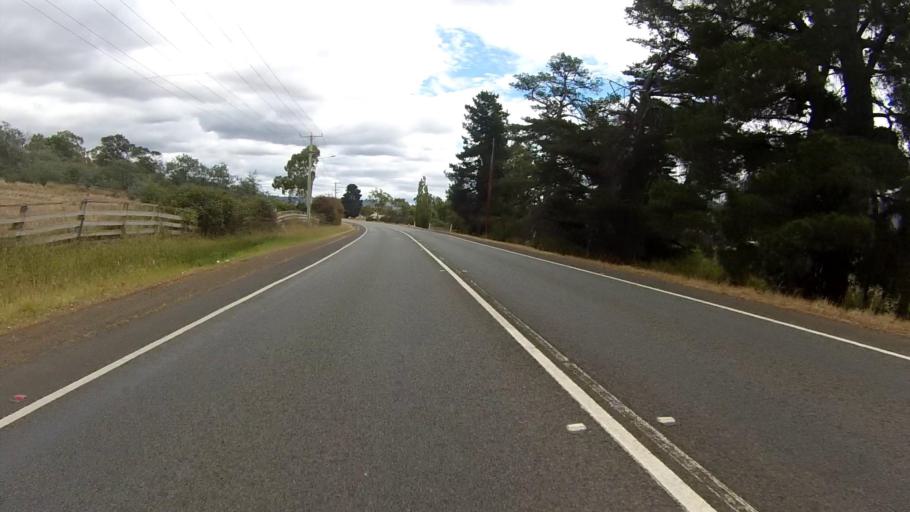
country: AU
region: Tasmania
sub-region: Brighton
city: Bridgewater
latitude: -42.6792
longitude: 147.2653
